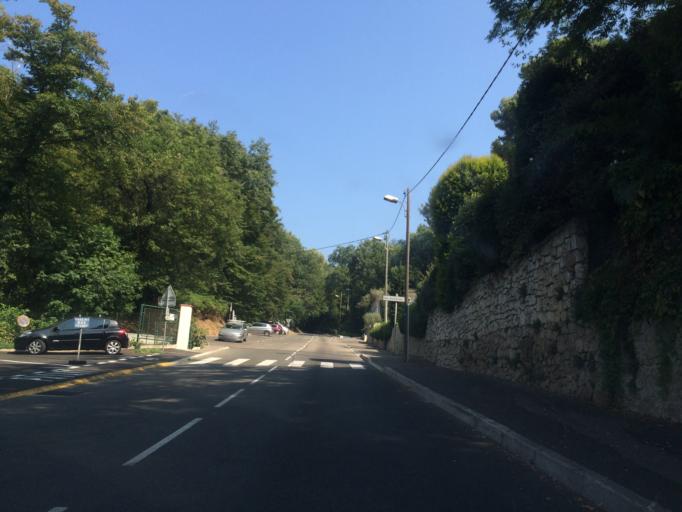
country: FR
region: Provence-Alpes-Cote d'Azur
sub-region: Departement des Alpes-Maritimes
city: Saint-Paul-de-Vence
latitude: 43.7000
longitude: 7.1179
